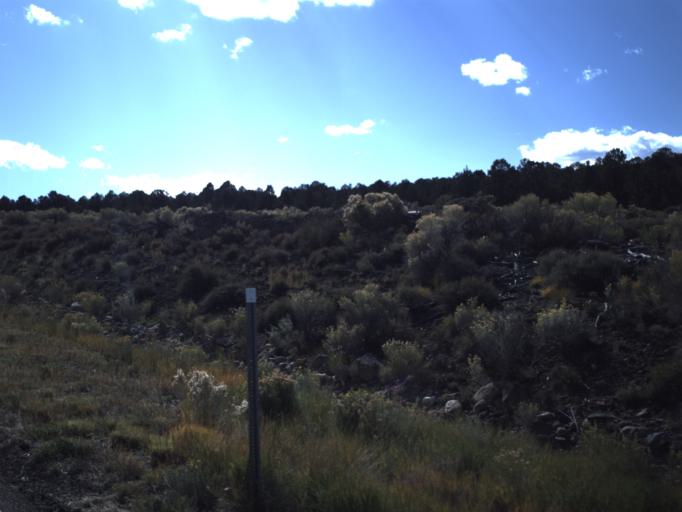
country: US
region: Utah
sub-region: Garfield County
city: Panguitch
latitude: 37.7793
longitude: -112.4417
